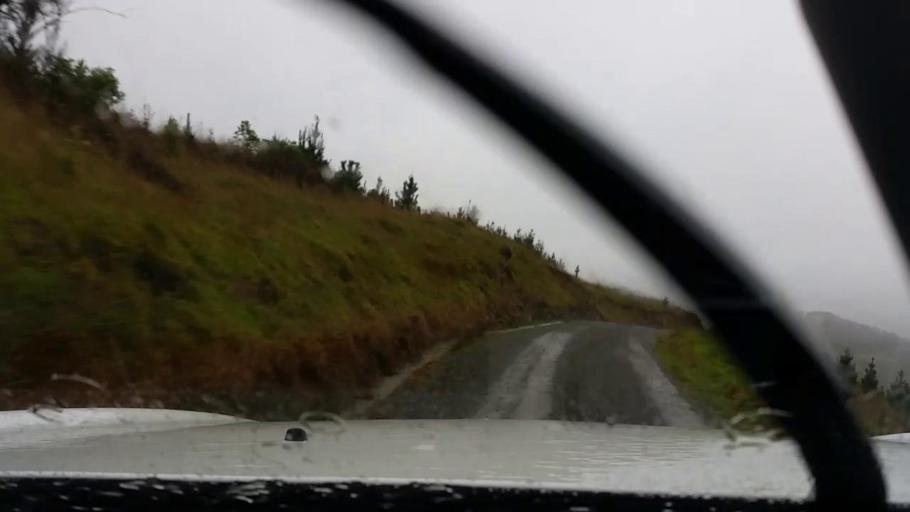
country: NZ
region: Wellington
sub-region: Masterton District
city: Masterton
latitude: -41.1947
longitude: 175.8098
